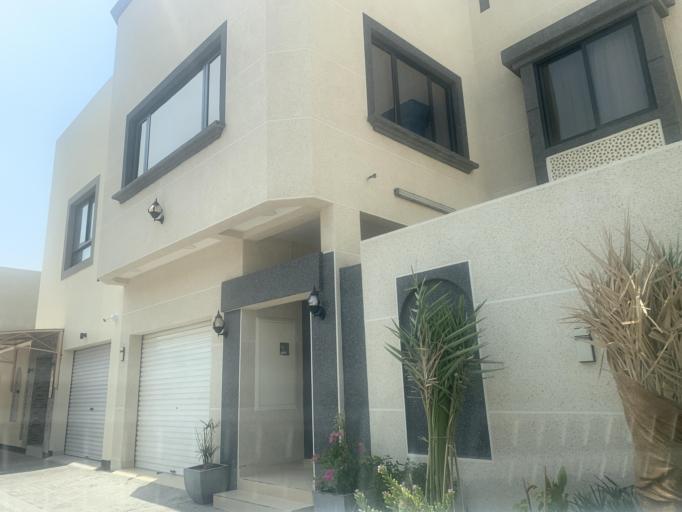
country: BH
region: Central Governorate
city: Madinat Hamad
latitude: 26.1635
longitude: 50.4528
